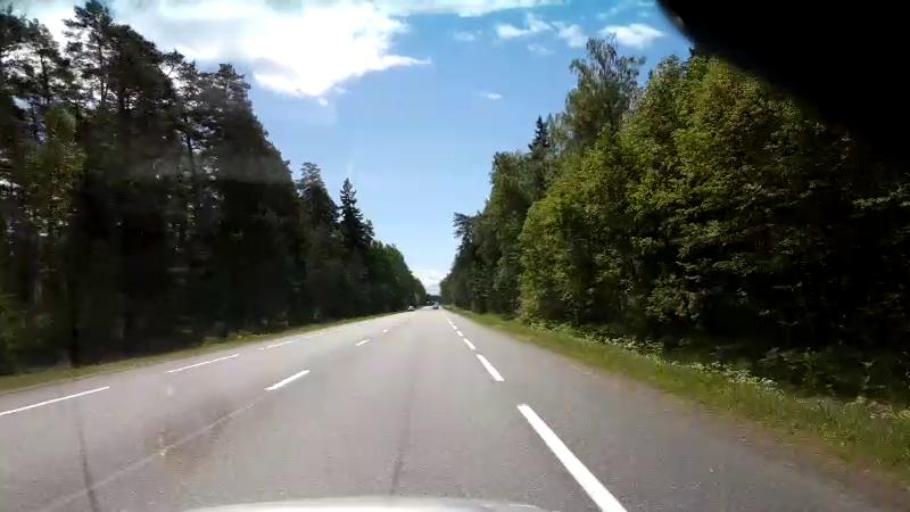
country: LV
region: Saulkrastu
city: Saulkrasti
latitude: 57.4778
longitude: 24.4337
